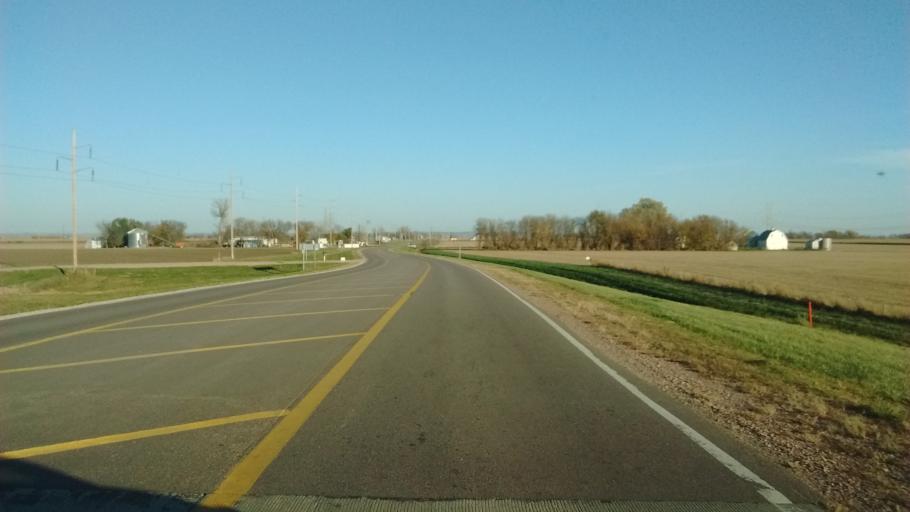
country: US
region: Iowa
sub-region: Woodbury County
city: Sergeant Bluff
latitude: 42.3299
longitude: -96.3155
